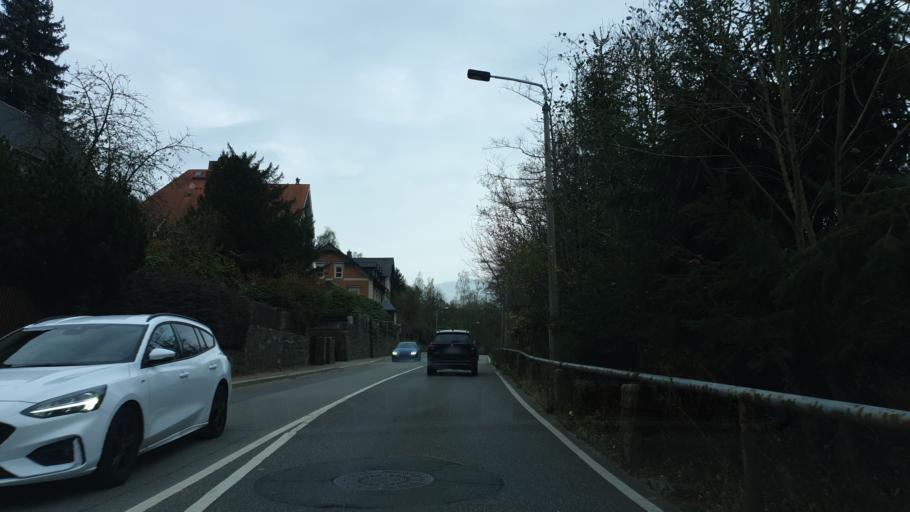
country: DE
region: Saxony
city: Schwarzenberg
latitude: 50.5322
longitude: 12.7857
